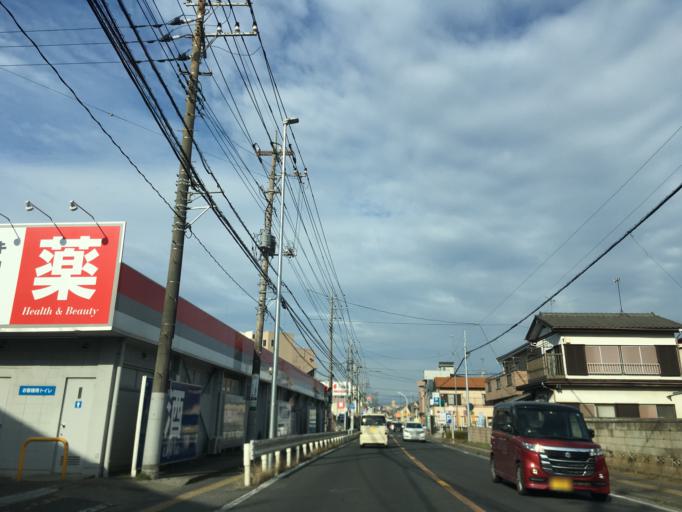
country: JP
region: Saitama
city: Sakado
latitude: 35.9082
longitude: 139.4144
